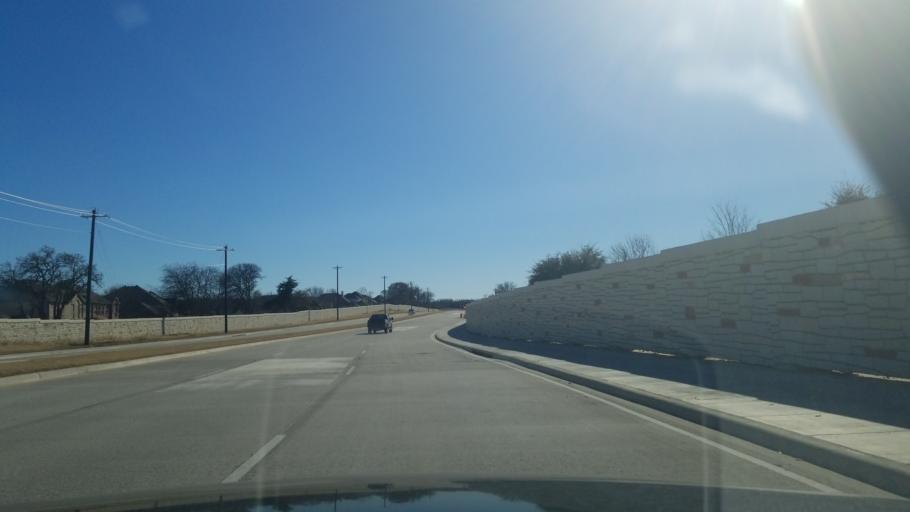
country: US
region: Texas
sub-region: Denton County
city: Corinth
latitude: 33.1497
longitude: -97.0976
